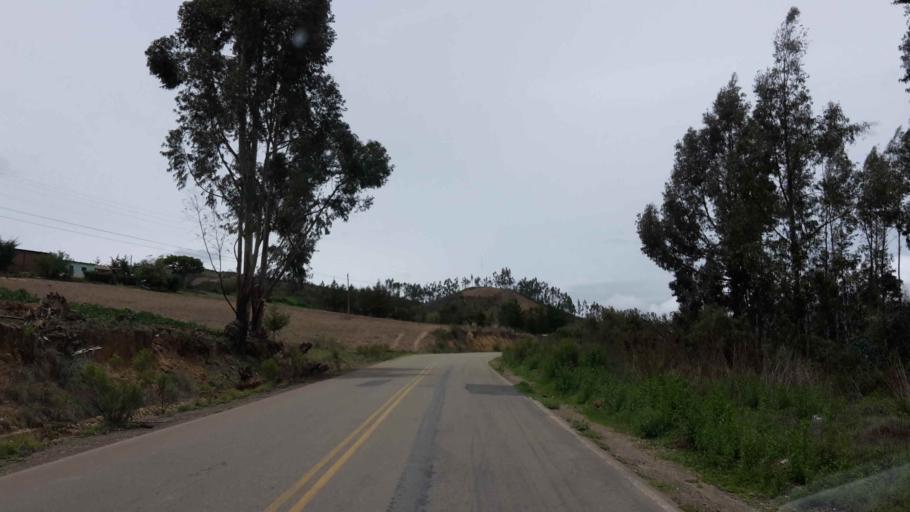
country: BO
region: Cochabamba
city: Totora
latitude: -17.6894
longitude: -65.2148
